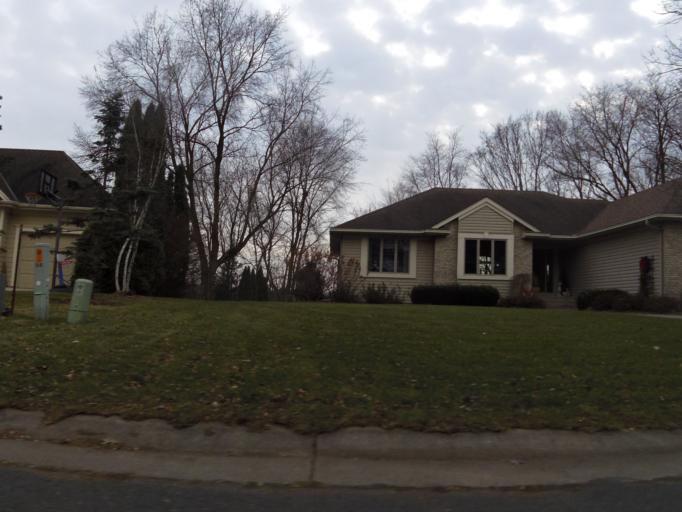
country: US
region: Wisconsin
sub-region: Pierce County
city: River Falls
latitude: 44.8606
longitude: -92.6011
